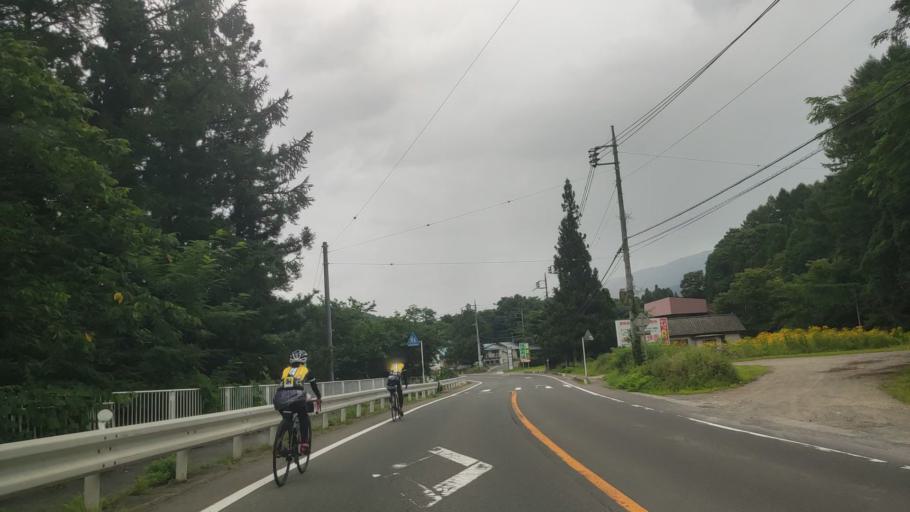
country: JP
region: Gunma
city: Numata
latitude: 36.7095
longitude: 139.2094
